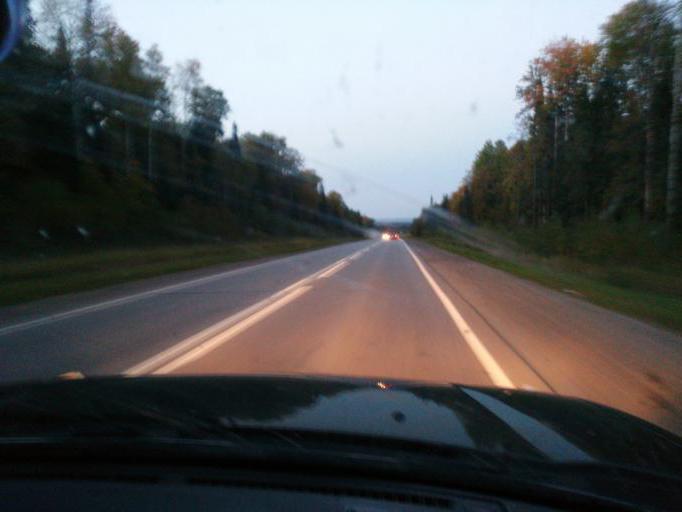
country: RU
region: Perm
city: Kalino
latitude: 58.2703
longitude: 57.3706
